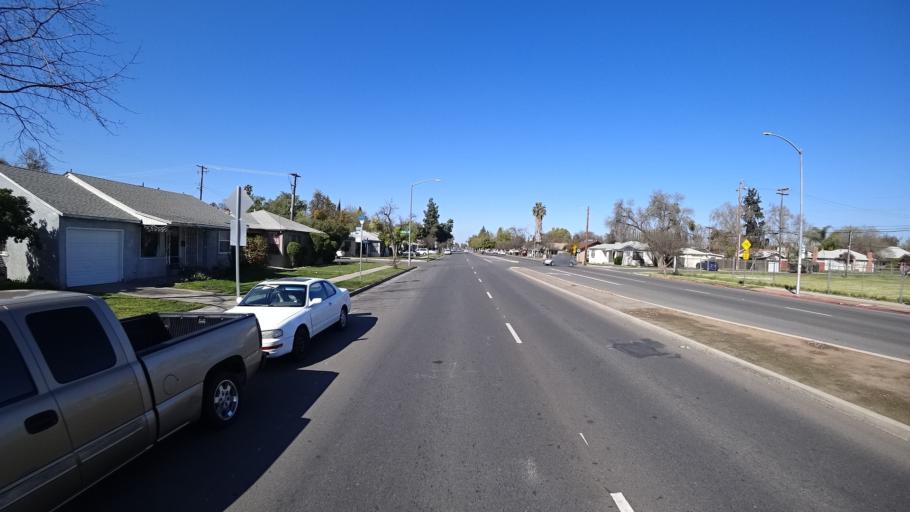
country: US
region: California
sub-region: Fresno County
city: Fresno
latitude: 36.7795
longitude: -119.7945
